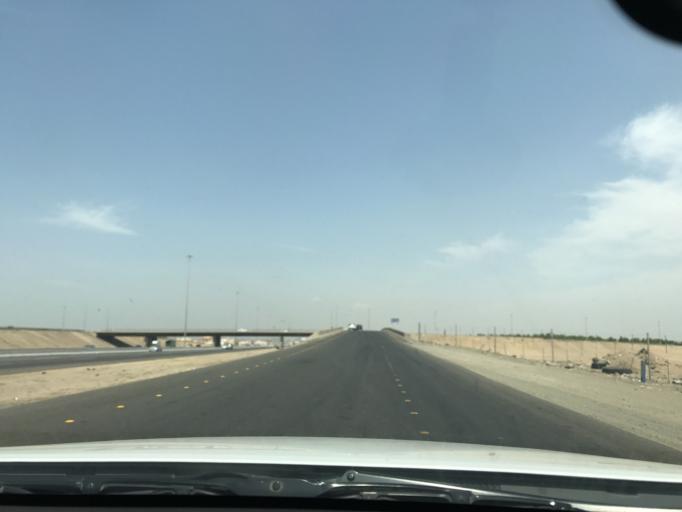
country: SA
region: Makkah
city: Jeddah
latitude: 21.3886
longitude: 39.4238
